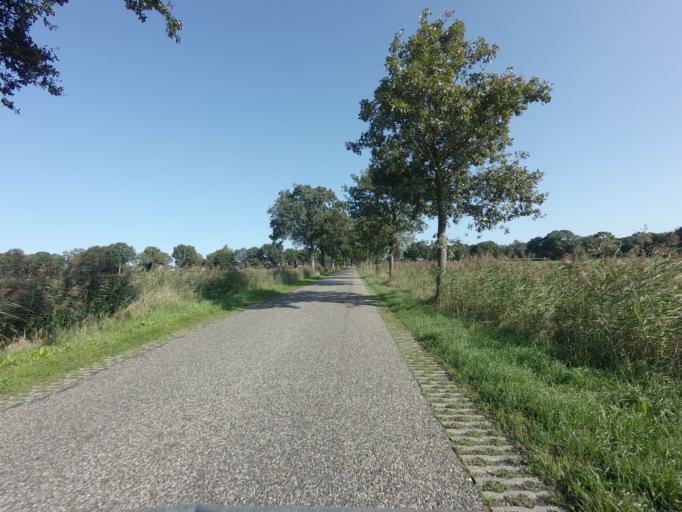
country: NL
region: Overijssel
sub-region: Gemeente Raalte
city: Raalte
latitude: 52.4370
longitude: 6.3020
